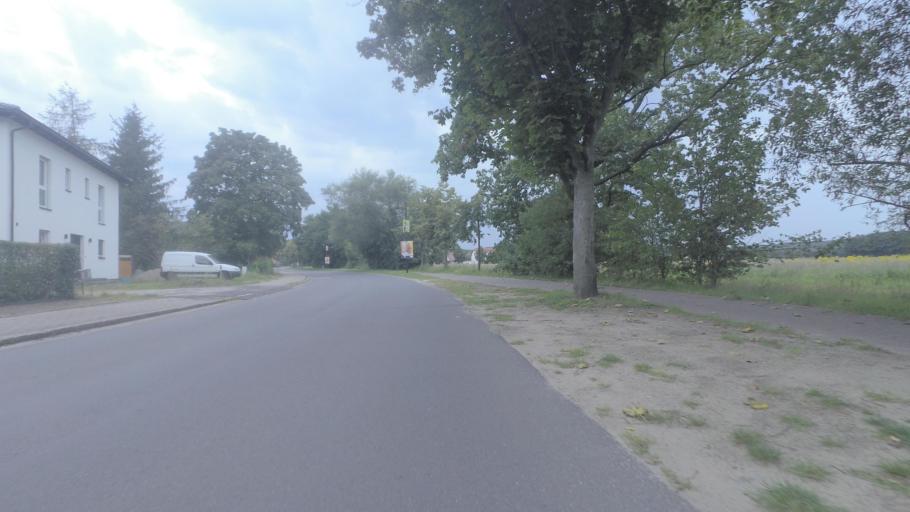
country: DE
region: Brandenburg
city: Potsdam
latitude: 52.3445
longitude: 13.1021
